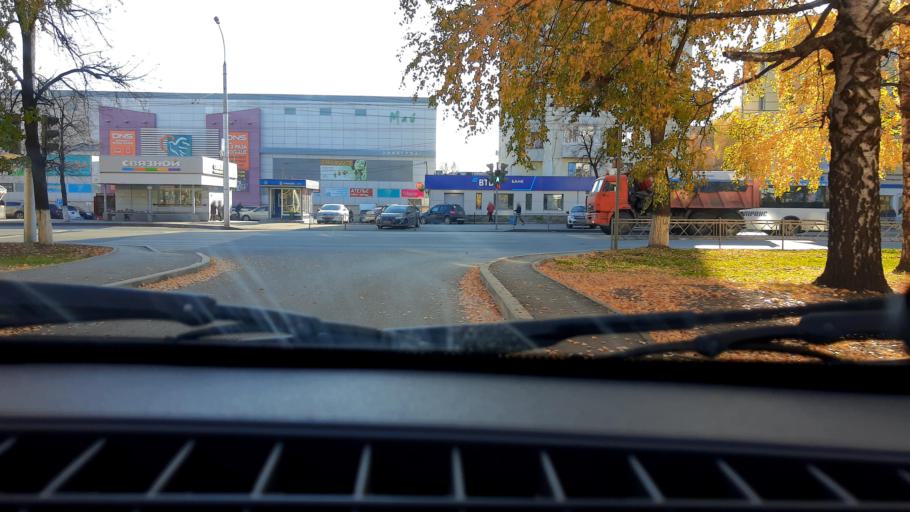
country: RU
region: Bashkortostan
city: Ufa
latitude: 54.8129
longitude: 56.0924
